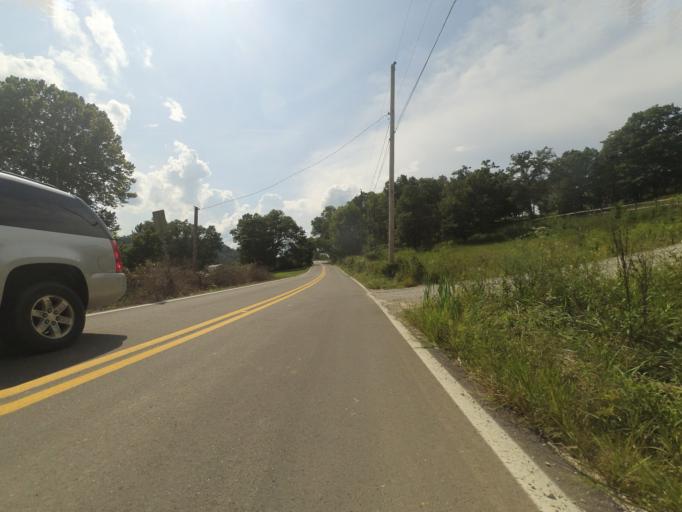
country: US
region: West Virginia
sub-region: Wayne County
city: Ceredo
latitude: 38.3735
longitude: -82.5363
